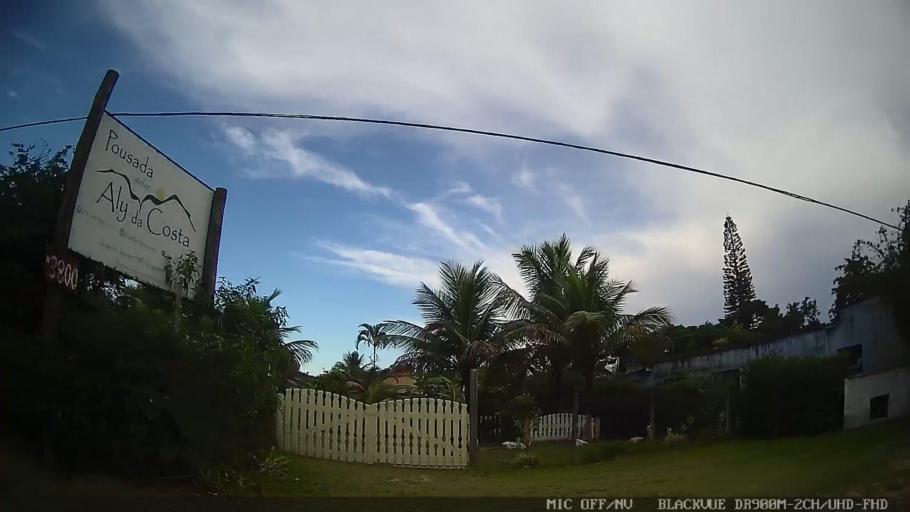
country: BR
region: Sao Paulo
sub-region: Iguape
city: Iguape
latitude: -24.6762
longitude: -47.4537
